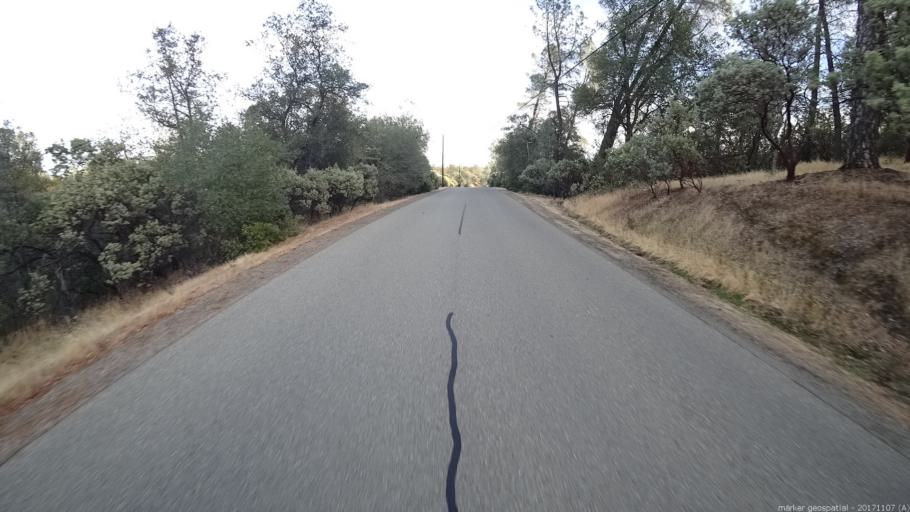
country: US
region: California
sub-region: Shasta County
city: Shasta
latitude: 40.5353
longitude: -122.4868
